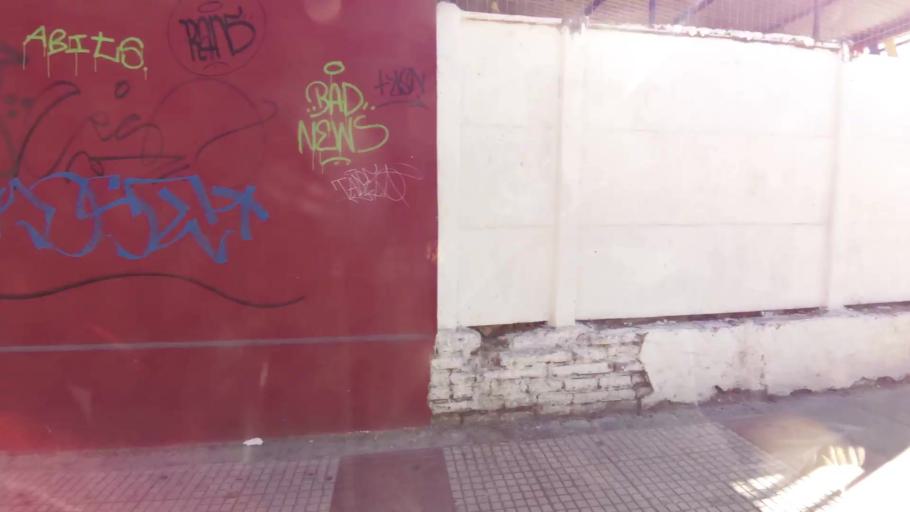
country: CL
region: O'Higgins
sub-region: Provincia de Cachapoal
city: Rancagua
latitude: -34.1714
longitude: -70.7408
